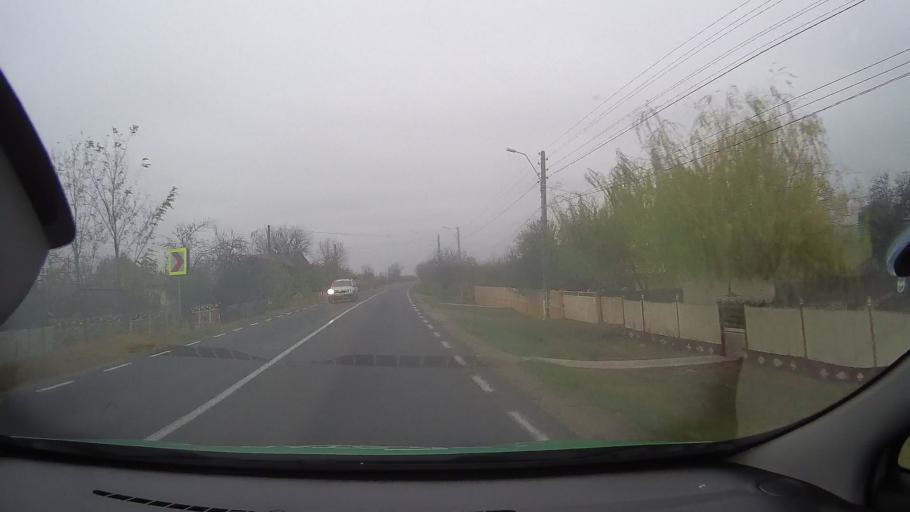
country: RO
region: Braila
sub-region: Comuna Baraganul
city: Baraganul
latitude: 44.7997
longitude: 27.5131
